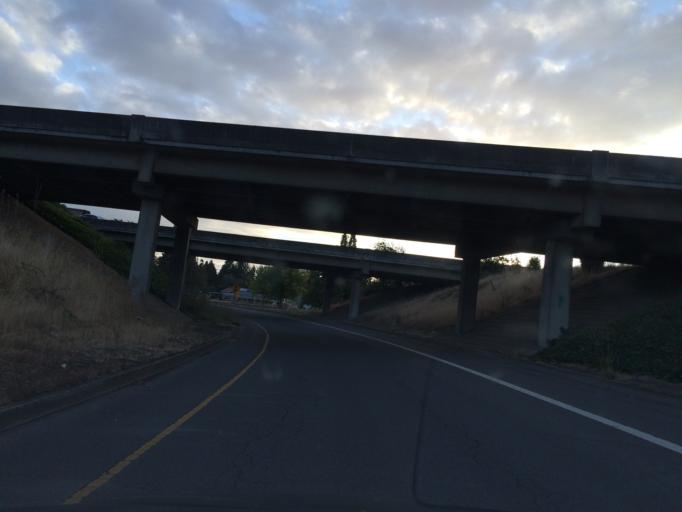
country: US
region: Oregon
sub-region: Linn County
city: Millersburg
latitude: 44.6448
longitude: -123.0619
